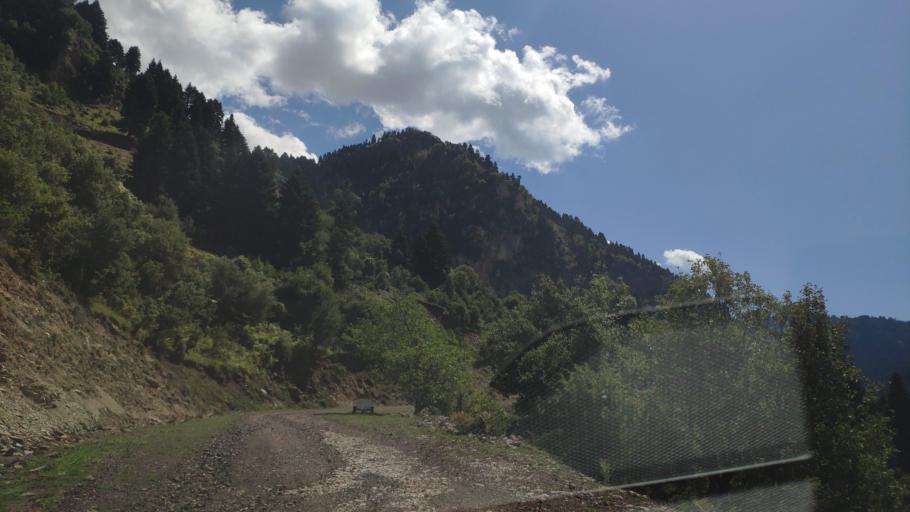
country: GR
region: Central Greece
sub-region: Nomos Evrytanias
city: Kerasochori
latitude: 39.1363
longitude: 21.6573
